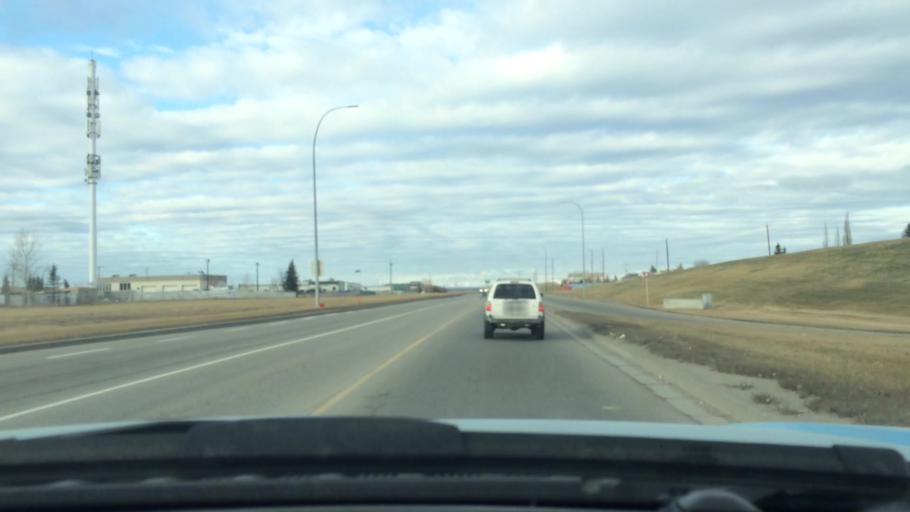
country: CA
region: Alberta
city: Calgary
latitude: 51.0150
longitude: -113.9775
